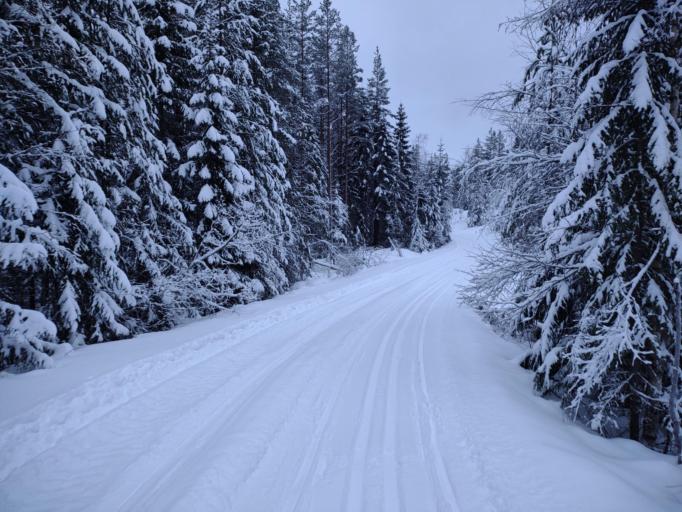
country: NO
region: Buskerud
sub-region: Flesberg
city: Lampeland
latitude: 59.7239
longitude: 9.5400
